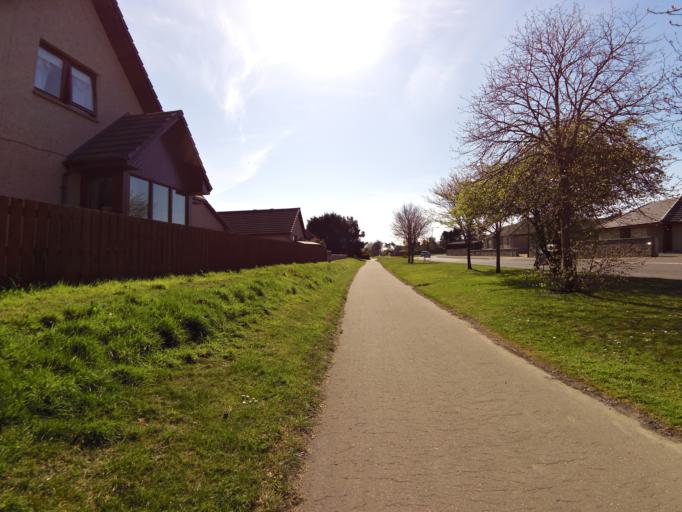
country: GB
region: Scotland
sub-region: Angus
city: Montrose
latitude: 56.7215
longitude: -2.4613
